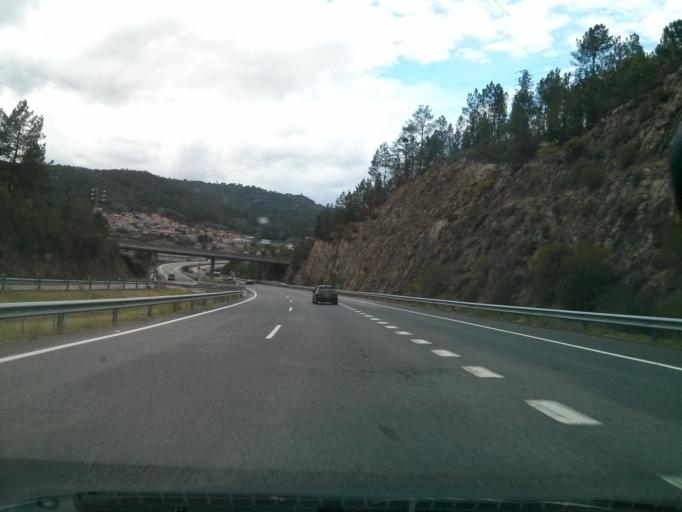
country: ES
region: Galicia
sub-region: Provincia de Ourense
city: Ourense
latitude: 42.3097
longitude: -7.8778
